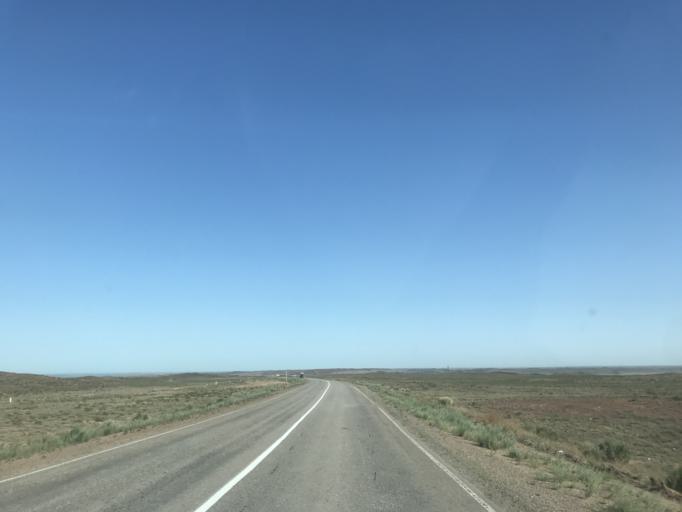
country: KZ
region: Zhambyl
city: Mynaral
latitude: 45.4715
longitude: 73.5562
